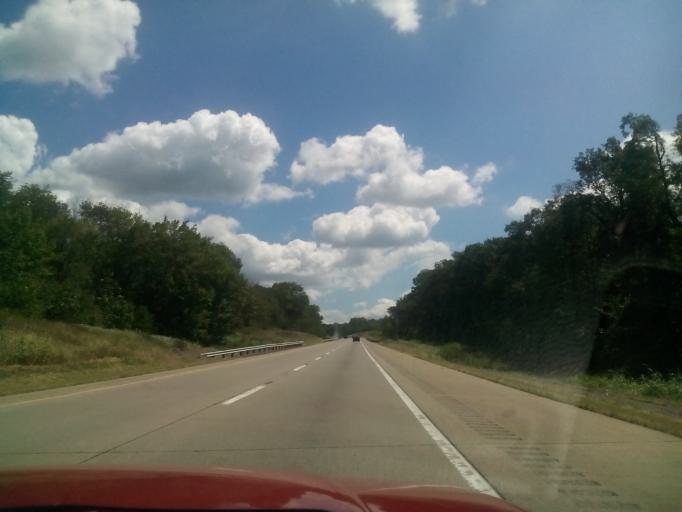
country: US
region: Pennsylvania
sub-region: Northumberland County
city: Riverside
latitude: 40.9877
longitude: -76.7255
